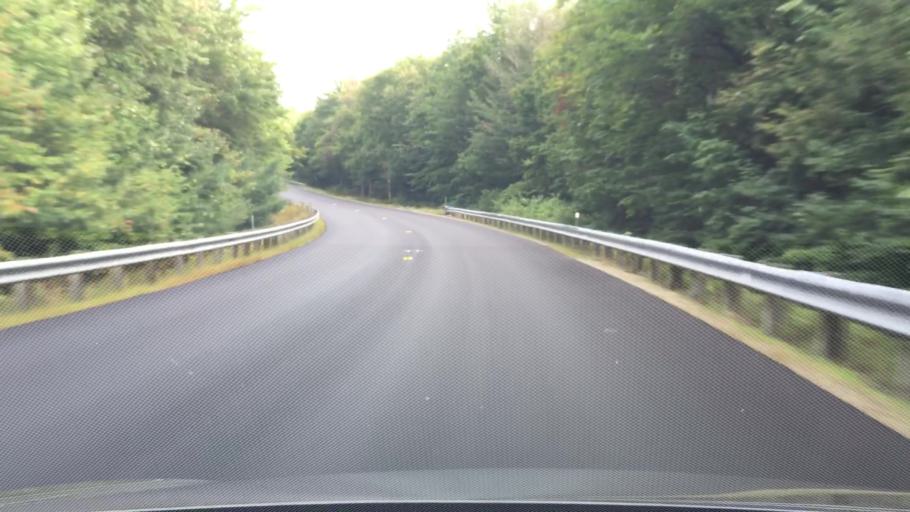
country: US
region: New Hampshire
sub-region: Carroll County
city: Sandwich
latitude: 44.0057
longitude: -71.4239
